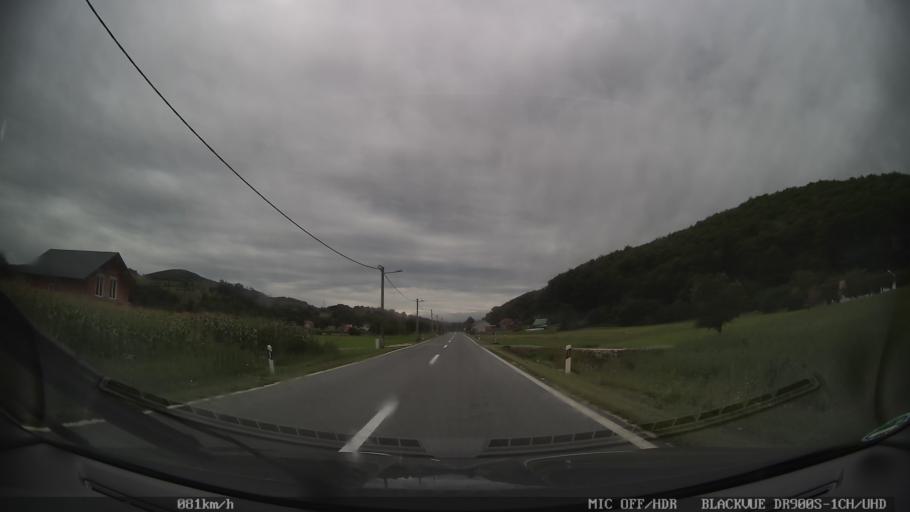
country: HR
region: Licko-Senjska
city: Brinje
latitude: 44.9347
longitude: 15.1300
